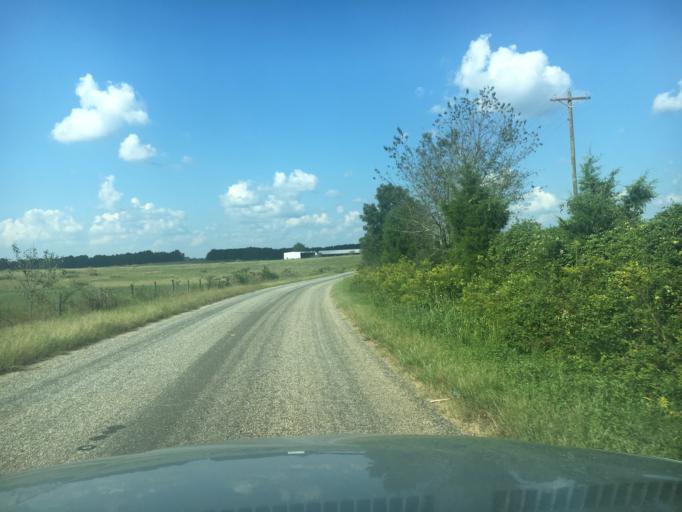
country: US
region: South Carolina
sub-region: Greenwood County
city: Ware Shoals
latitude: 34.4792
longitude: -82.2416
